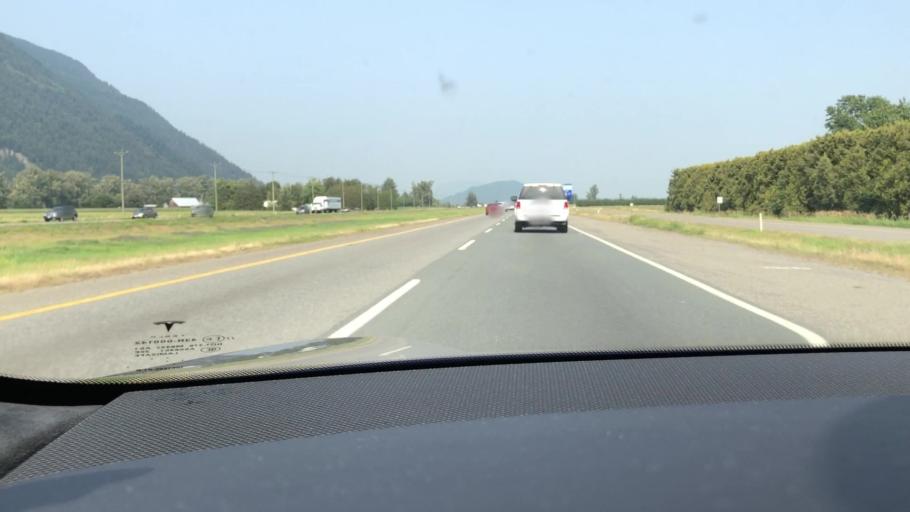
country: CA
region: British Columbia
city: Abbotsford
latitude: 49.0752
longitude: -122.1475
